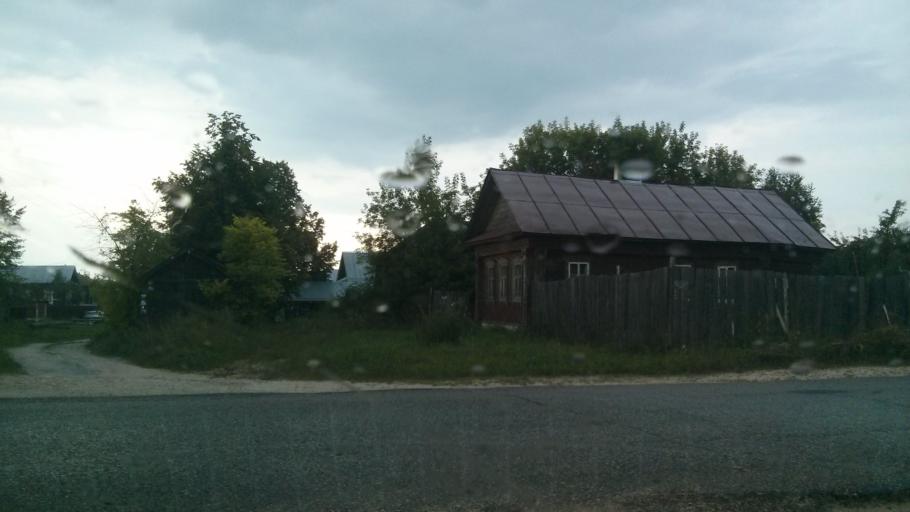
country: RU
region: Nizjnij Novgorod
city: Shimorskoye
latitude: 55.3404
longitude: 41.8602
